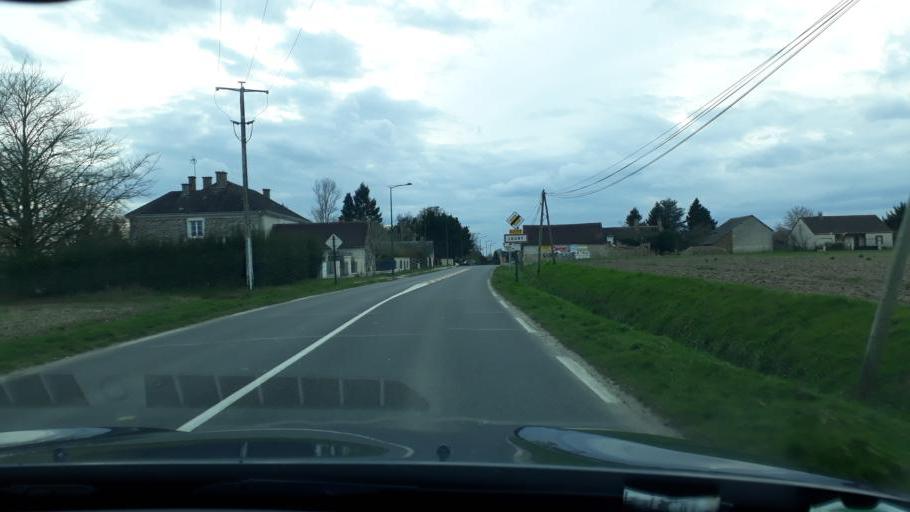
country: FR
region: Centre
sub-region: Departement du Loiret
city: Loury
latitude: 48.0057
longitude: 2.1007
